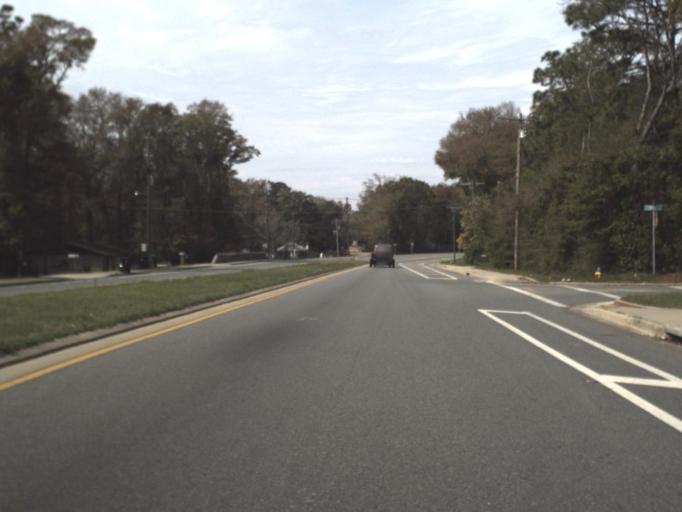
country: US
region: Florida
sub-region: Leon County
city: Tallahassee
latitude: 30.3761
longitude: -84.2953
